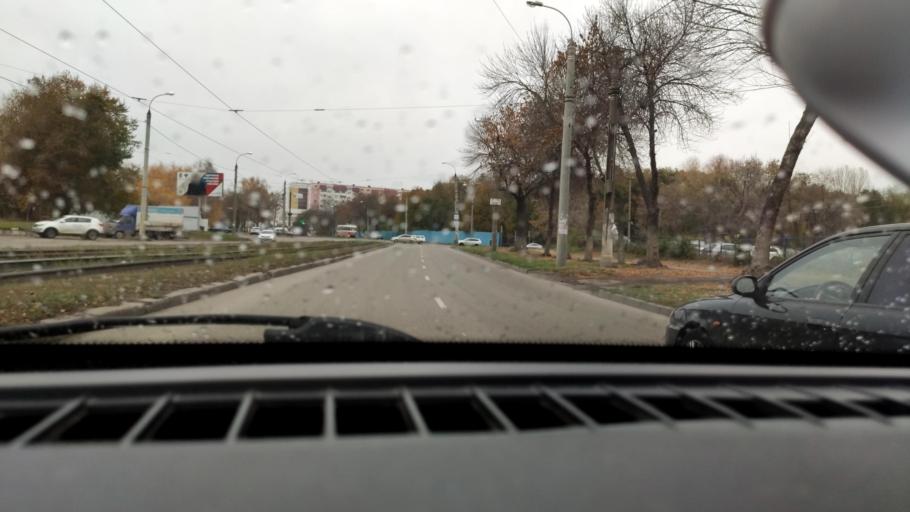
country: RU
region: Samara
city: Samara
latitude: 53.2245
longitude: 50.2340
